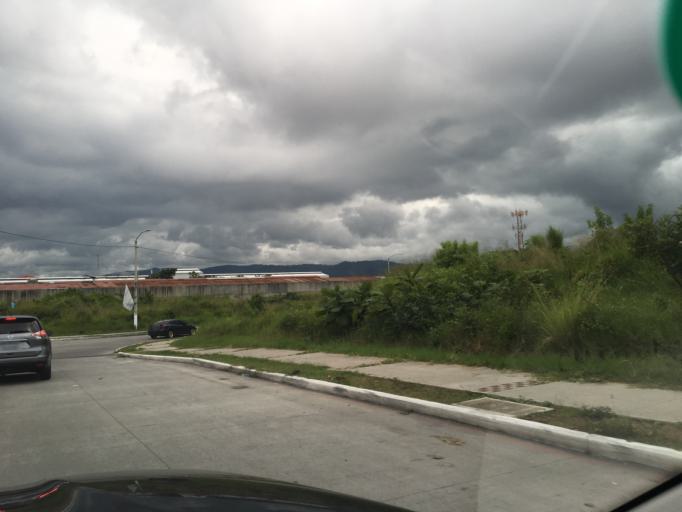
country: GT
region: Guatemala
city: Villa Nueva
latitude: 14.5080
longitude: -90.5872
